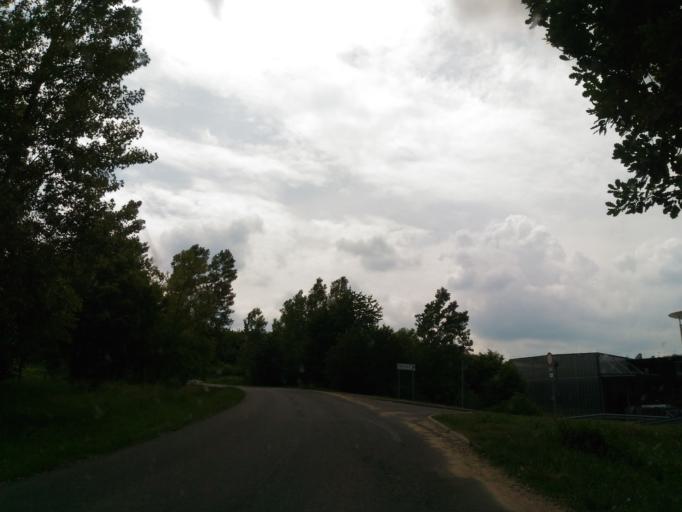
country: HU
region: Baranya
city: Komlo
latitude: 46.1862
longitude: 18.2394
